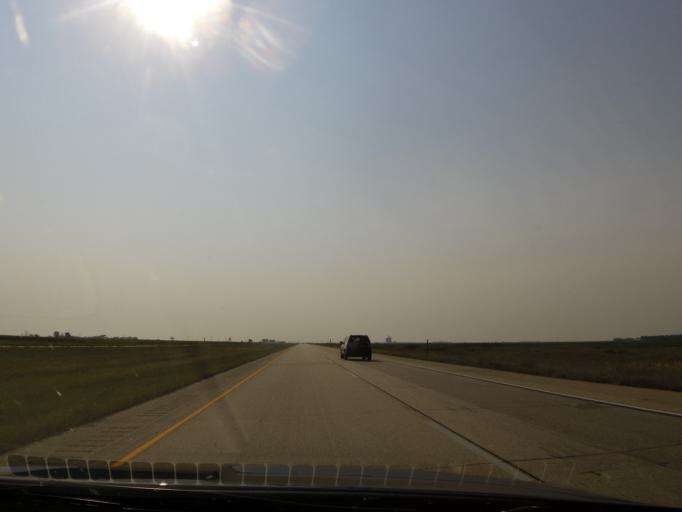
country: US
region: North Dakota
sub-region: Traill County
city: Hillsboro
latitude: 47.3905
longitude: -97.0664
